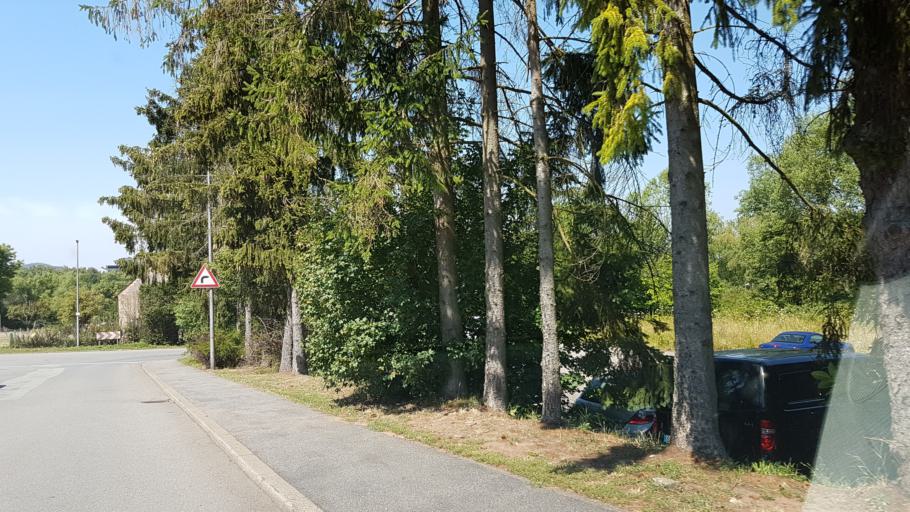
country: DE
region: Saarland
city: Homburg
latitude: 49.3123
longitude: 7.3320
